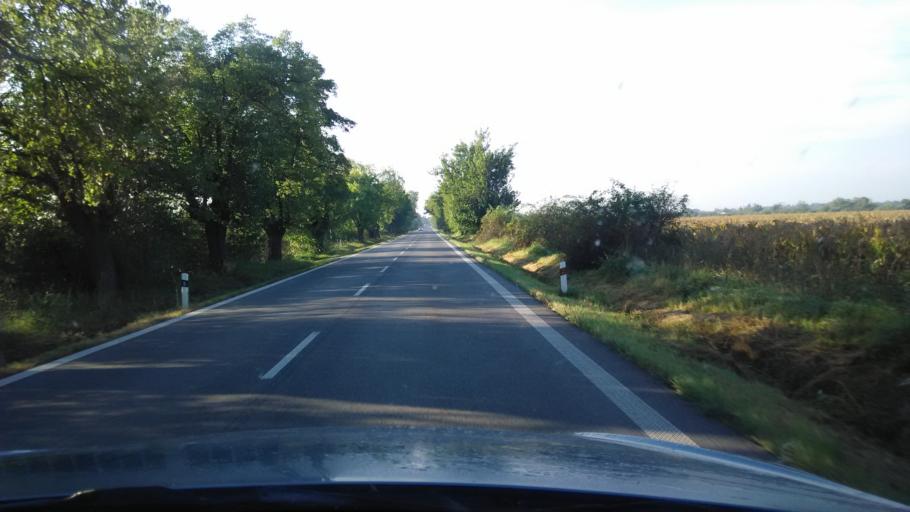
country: SK
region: Nitriansky
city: Tlmace
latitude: 48.2602
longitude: 18.5128
